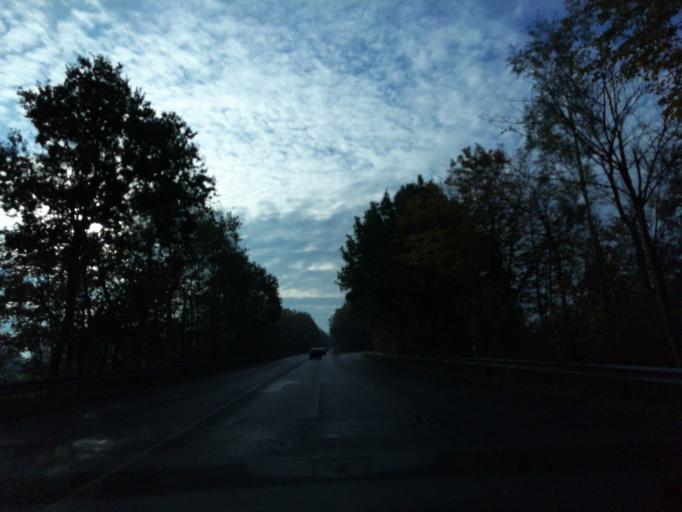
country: DE
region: Lower Saxony
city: Fedderwarden
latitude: 53.5972
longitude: 8.0517
